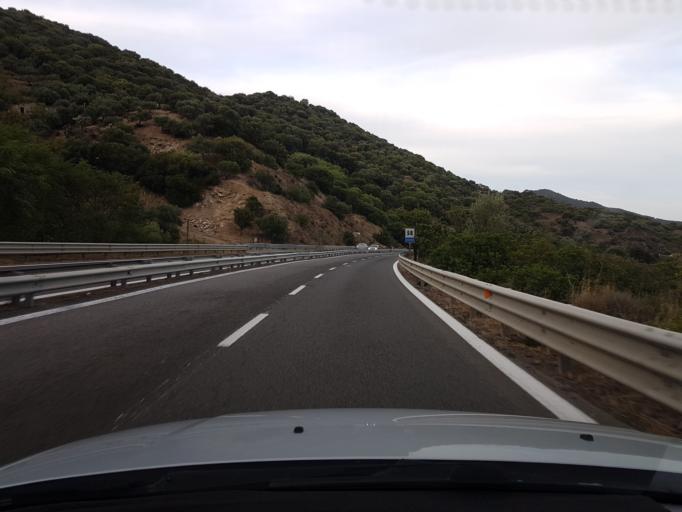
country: IT
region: Sardinia
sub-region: Provincia di Nuoro
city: Orune
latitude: 40.3598
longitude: 9.3527
